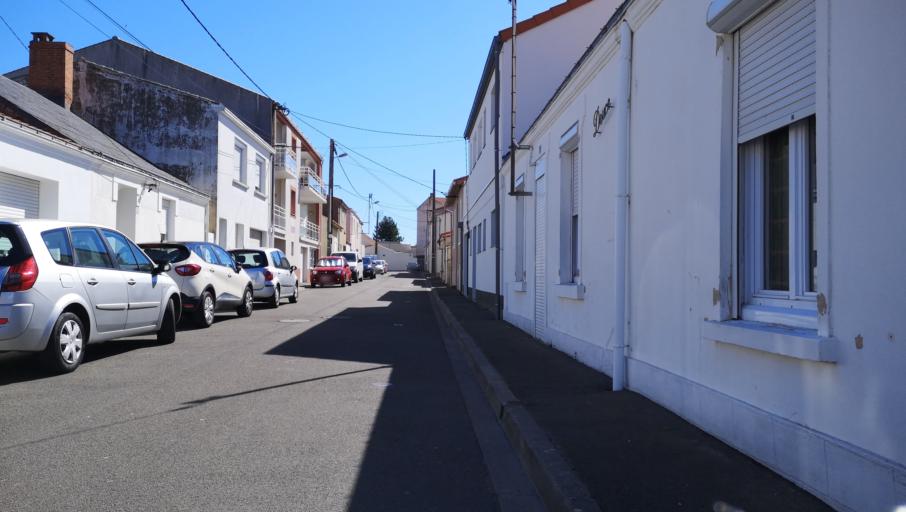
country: FR
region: Pays de la Loire
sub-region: Departement de la Vendee
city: Les Sables-d'Olonne
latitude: 46.5031
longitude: -1.7818
